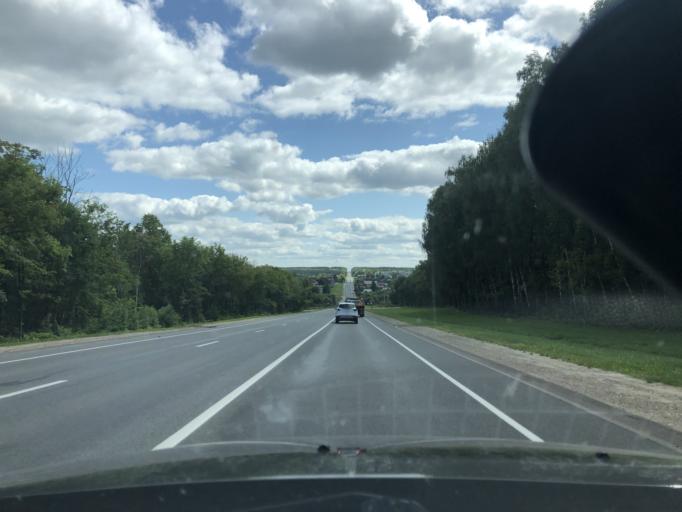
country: RU
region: Tula
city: Gorelki
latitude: 54.3096
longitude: 37.5680
